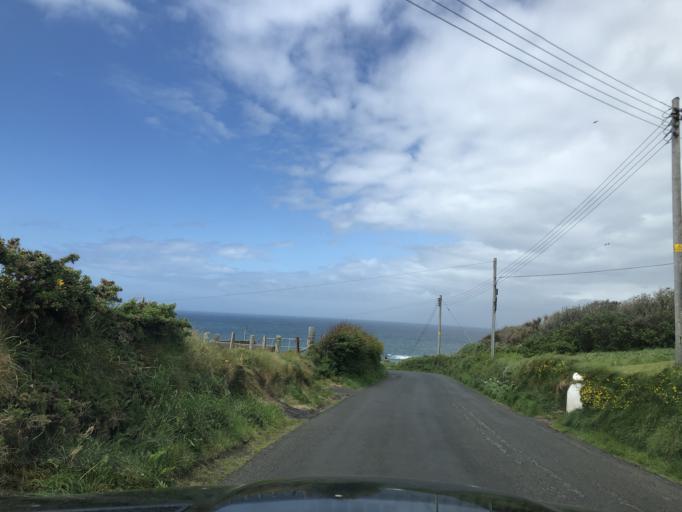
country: GB
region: Northern Ireland
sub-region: Moyle District
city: Ballycastle
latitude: 55.2428
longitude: -6.3678
